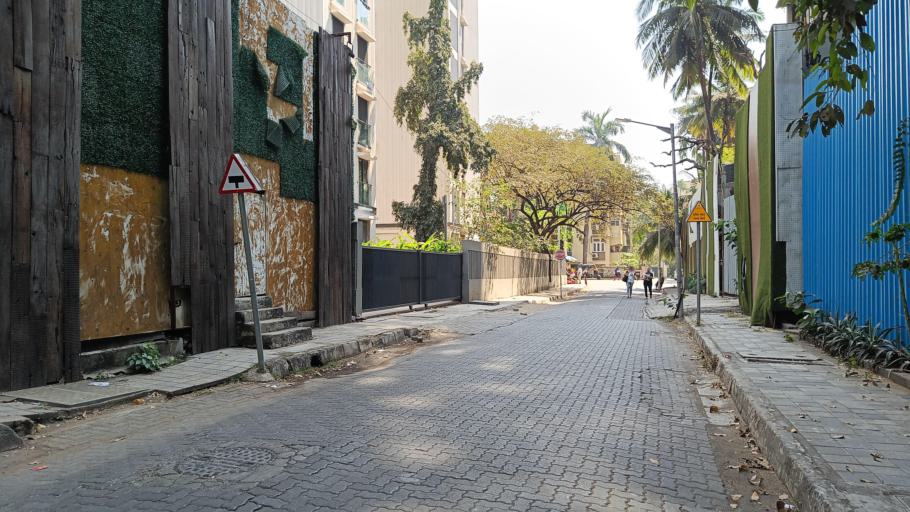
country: IN
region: Maharashtra
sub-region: Mumbai Suburban
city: Mumbai
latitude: 19.0570
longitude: 72.8496
